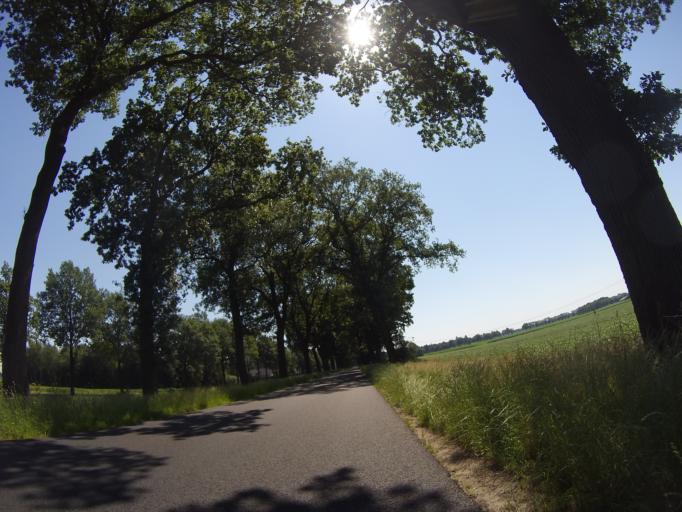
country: NL
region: Drenthe
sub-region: Gemeente Coevorden
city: Sleen
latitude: 52.8306
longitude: 6.8128
